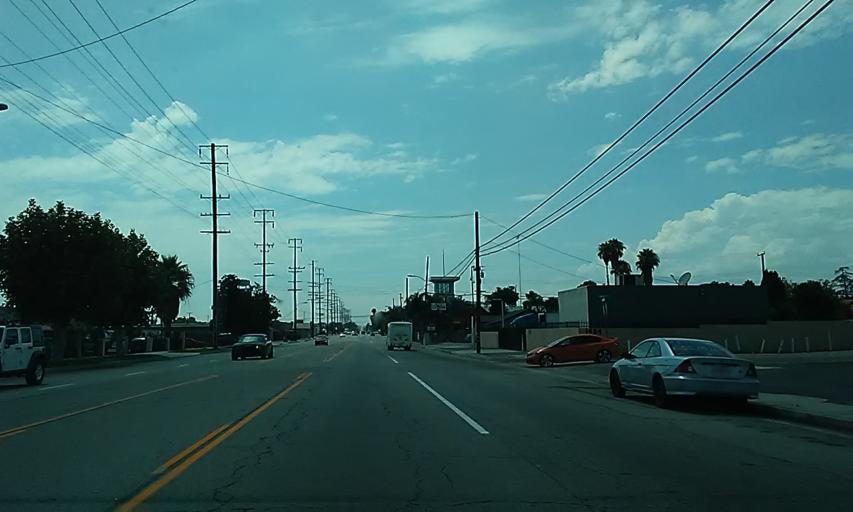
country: US
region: California
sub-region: San Bernardino County
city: San Bernardino
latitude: 34.1214
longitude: -117.2556
